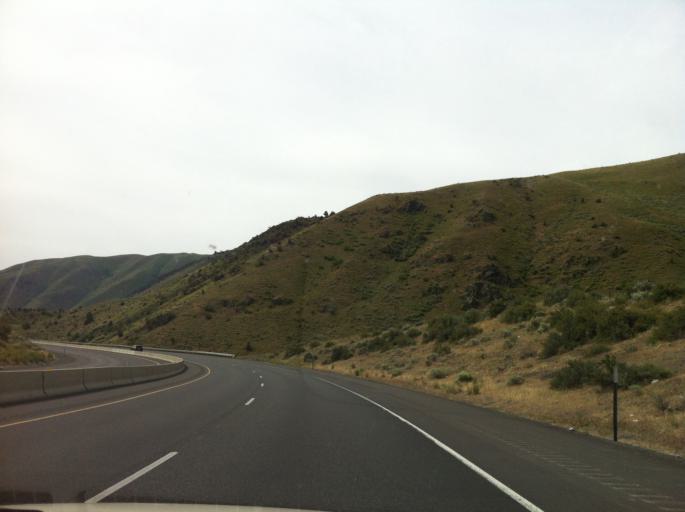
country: US
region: Idaho
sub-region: Washington County
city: Weiser
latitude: 44.5124
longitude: -117.3762
